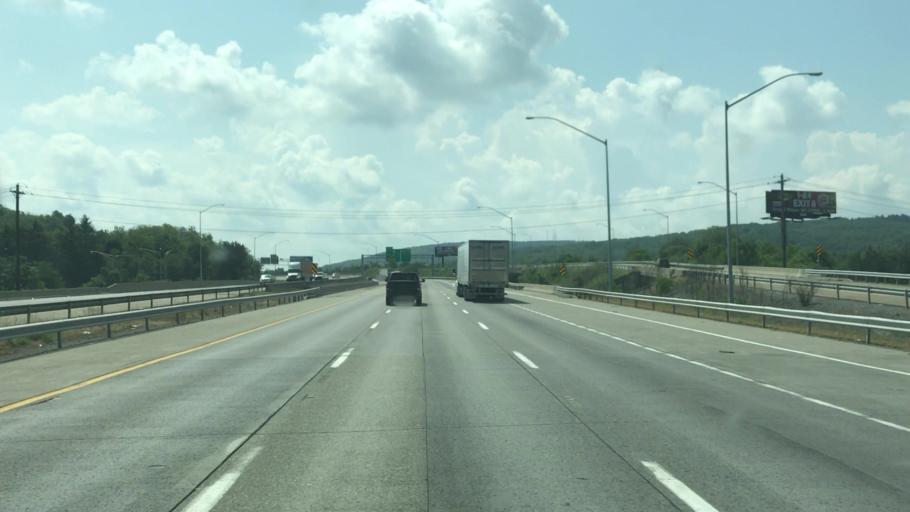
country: US
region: Pennsylvania
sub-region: Lackawanna County
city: Dunmore
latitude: 41.4146
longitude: -75.6011
